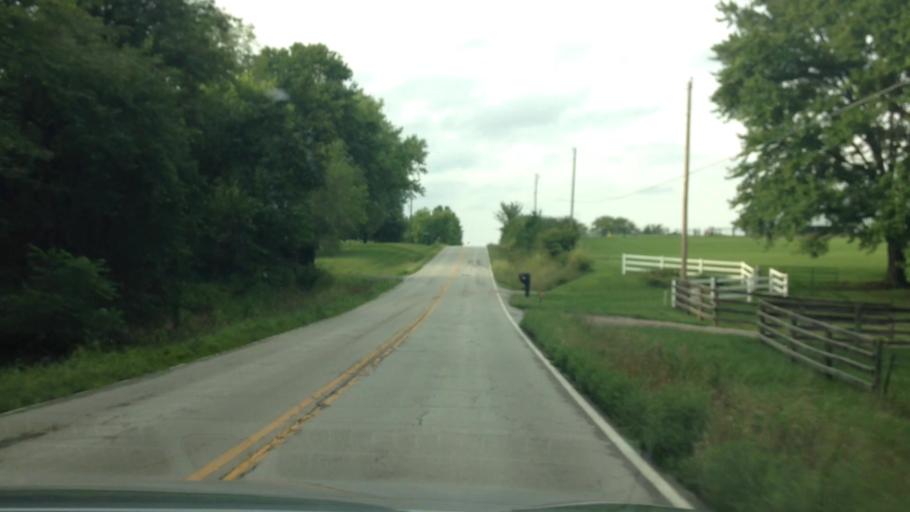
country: US
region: Missouri
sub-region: Clay County
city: Smithville
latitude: 39.3755
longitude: -94.6670
